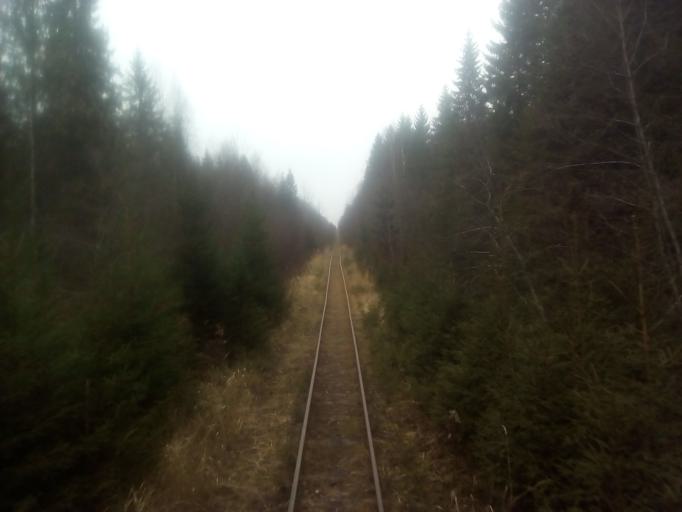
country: RU
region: Vologda
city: Kharovsk
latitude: 59.8093
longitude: 40.2655
